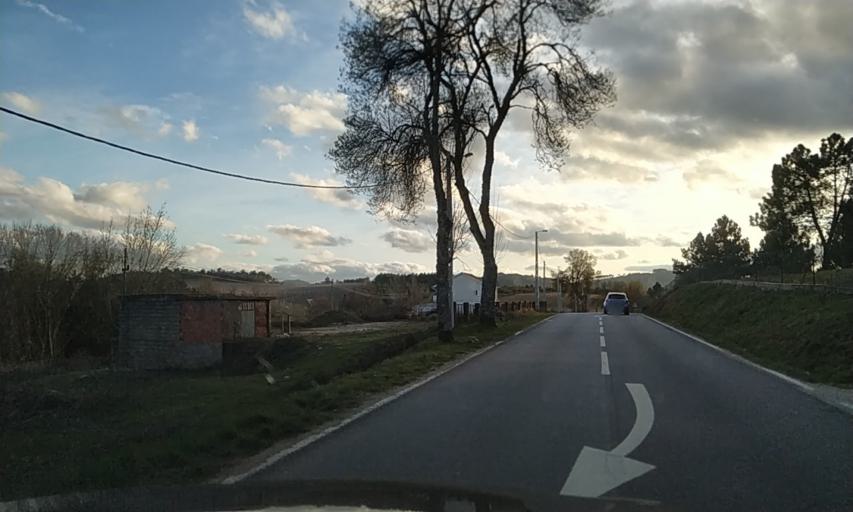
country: PT
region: Braganca
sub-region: Carrazeda de Ansiaes
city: Carrazeda de Anciaes
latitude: 41.2316
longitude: -7.3268
